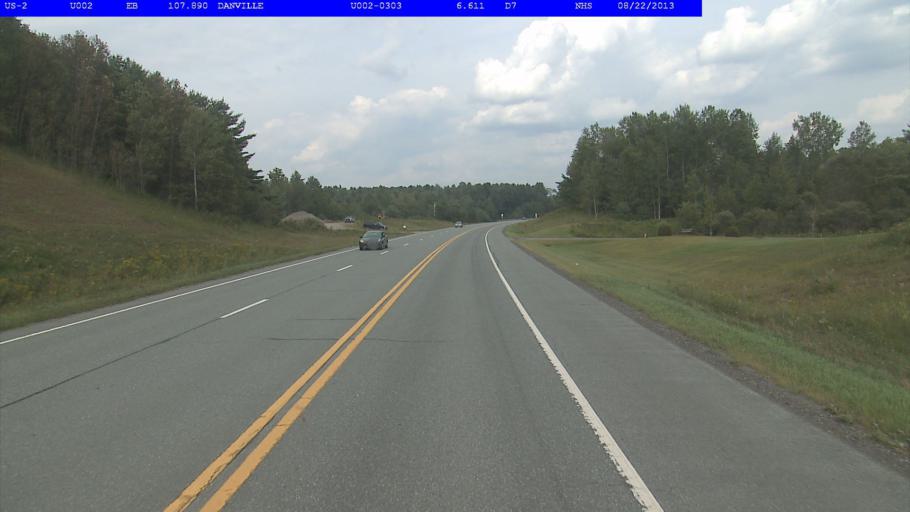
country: US
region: Vermont
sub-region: Caledonia County
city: St Johnsbury
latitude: 44.4289
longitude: -72.1047
